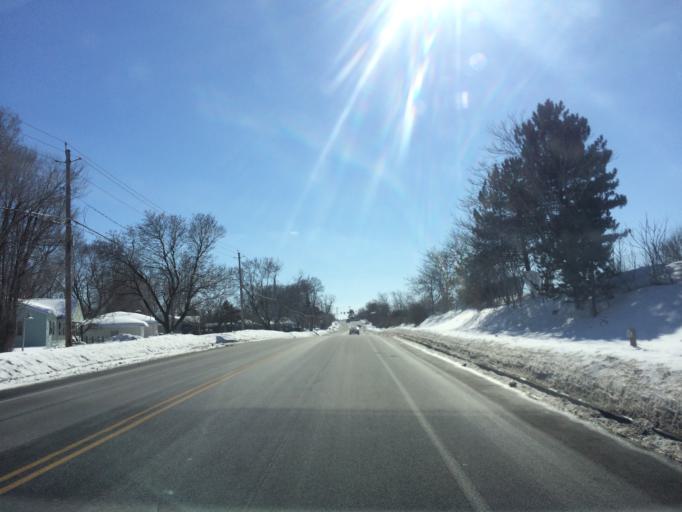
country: US
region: New York
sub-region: Monroe County
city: Rochester
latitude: 43.0986
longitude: -77.6001
